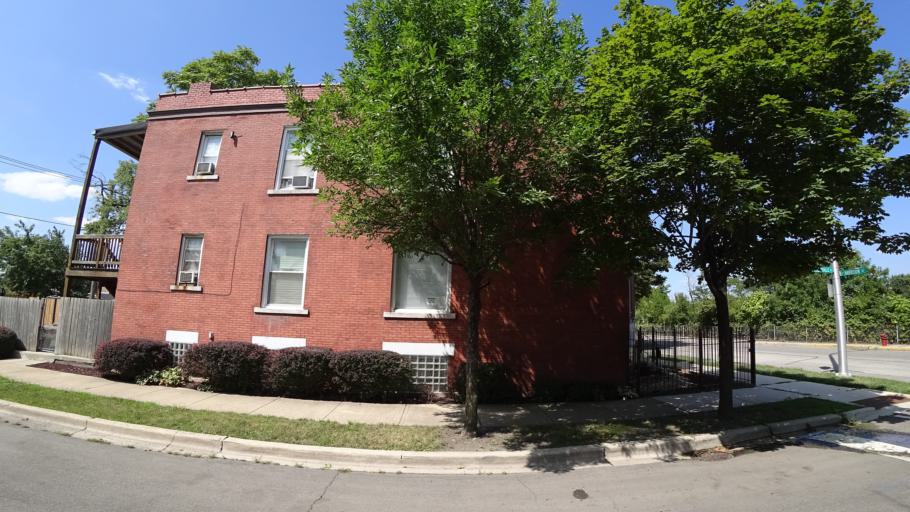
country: US
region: Illinois
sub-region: Cook County
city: Cicero
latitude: 41.8732
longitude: -87.7291
